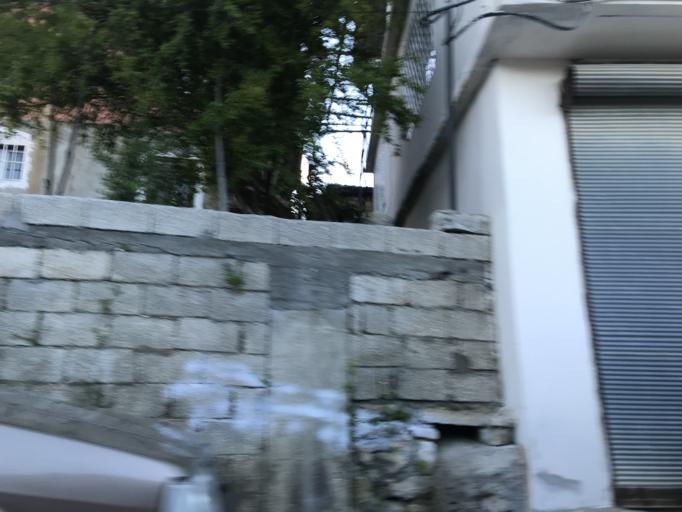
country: TR
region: Hatay
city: Buyukcat
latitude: 36.0999
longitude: 36.0568
